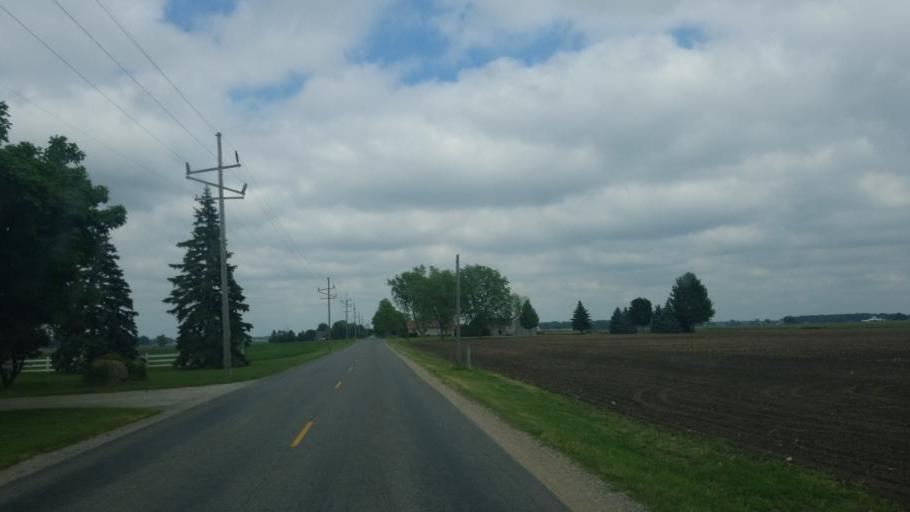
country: US
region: Indiana
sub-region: Elkhart County
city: Wakarusa
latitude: 41.4935
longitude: -86.0189
